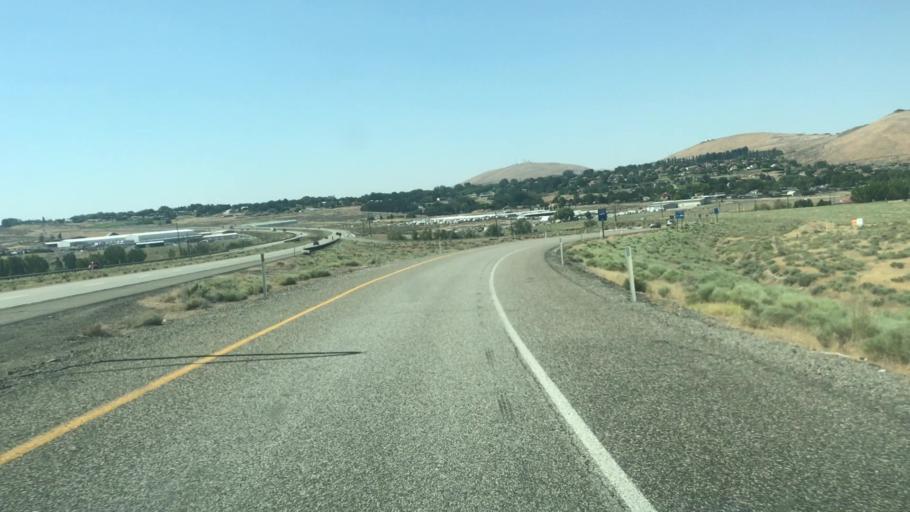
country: US
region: Washington
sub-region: Franklin County
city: West Pasco
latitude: 46.1917
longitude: -119.2618
